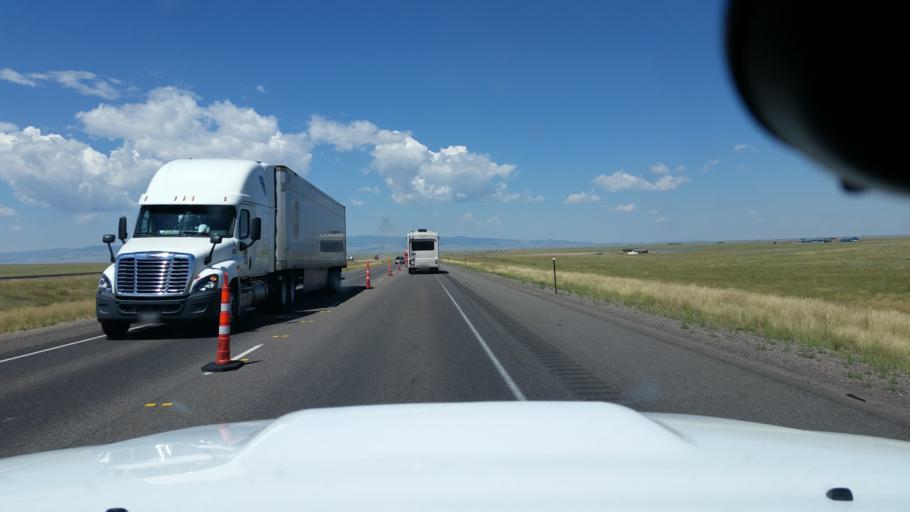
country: US
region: Wyoming
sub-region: Albany County
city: Laramie
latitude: 41.3580
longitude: -105.7558
